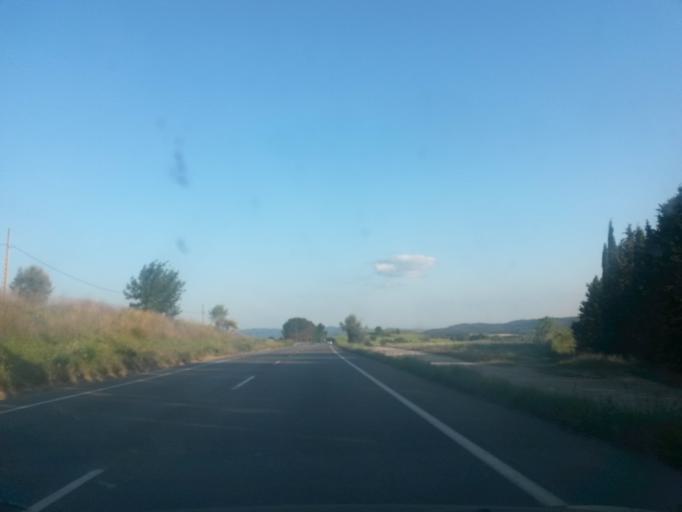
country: ES
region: Catalonia
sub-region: Provincia de Girona
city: Fontcoberta
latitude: 42.1164
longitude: 2.7891
